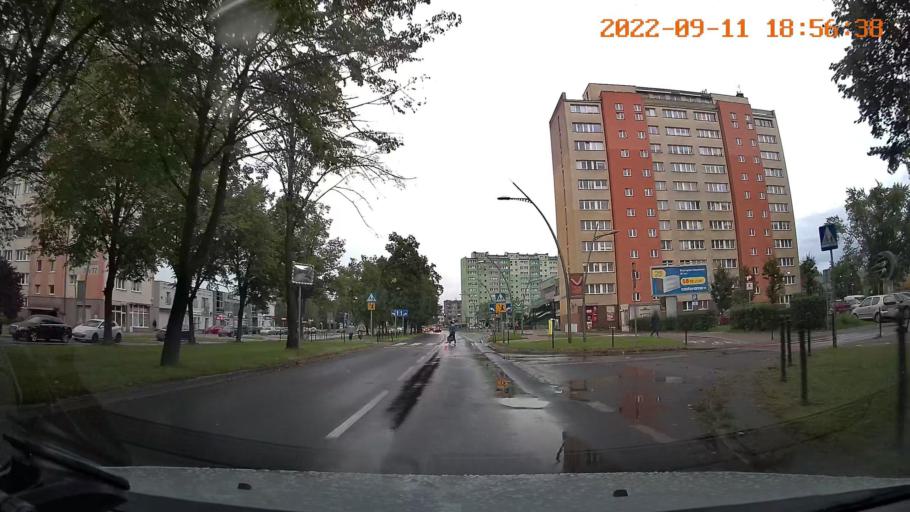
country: PL
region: Silesian Voivodeship
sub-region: Tychy
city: Cielmice
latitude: 50.1120
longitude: 19.0004
